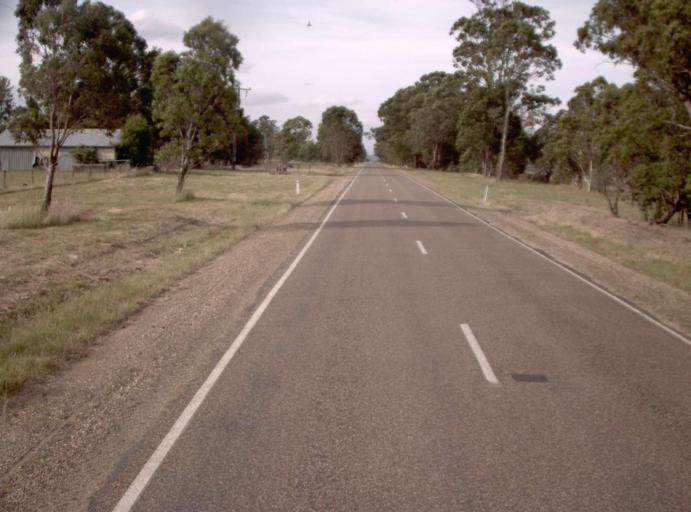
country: AU
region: Victoria
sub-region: Wellington
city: Heyfield
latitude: -38.0339
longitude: 146.6672
